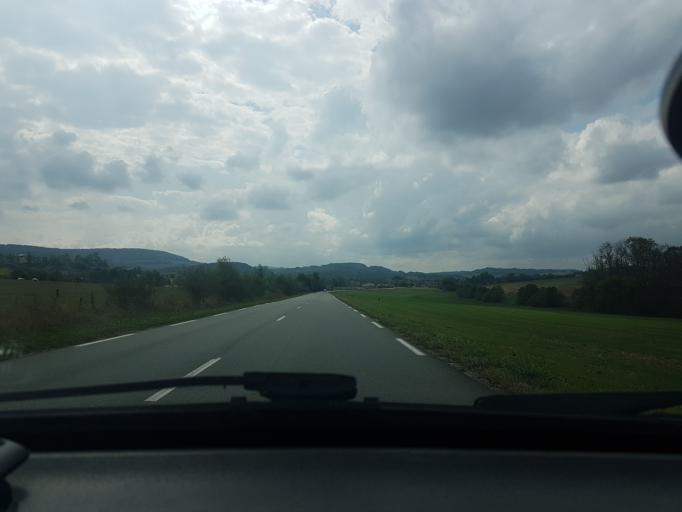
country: FR
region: Franche-Comte
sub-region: Departement du Doubs
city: Arcey
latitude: 47.5564
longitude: 6.5980
